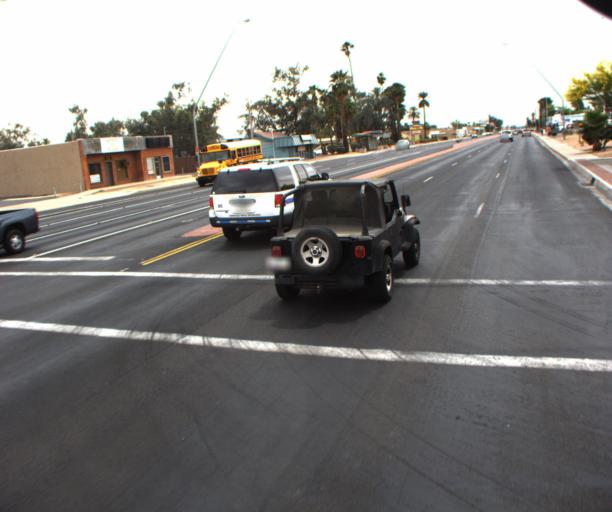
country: US
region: Arizona
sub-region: Maricopa County
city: Mesa
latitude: 33.4063
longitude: -111.8402
